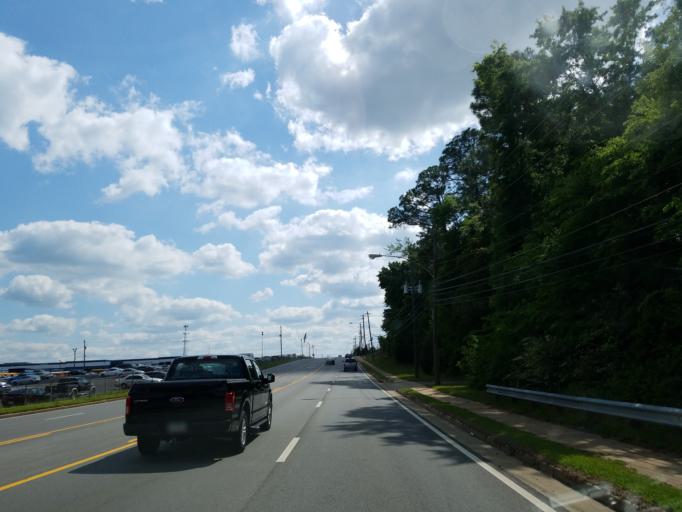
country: US
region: Georgia
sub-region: Peach County
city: Fort Valley
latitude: 32.5636
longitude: -83.8791
